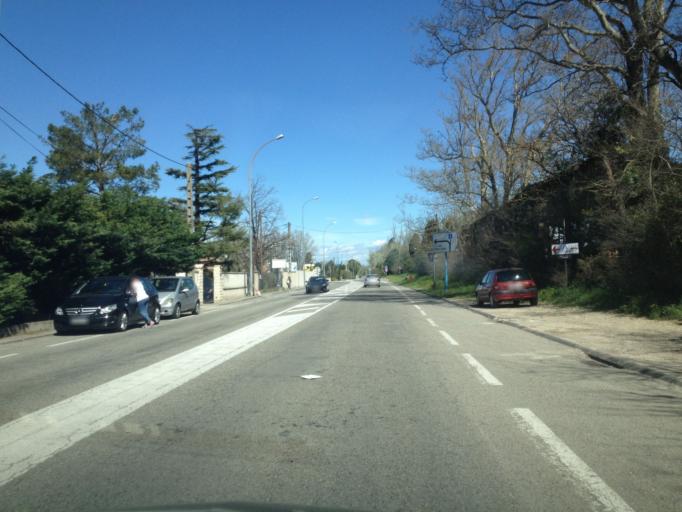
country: FR
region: Provence-Alpes-Cote d'Azur
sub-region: Departement du Vaucluse
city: Le Pontet
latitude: 43.9695
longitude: 4.8669
